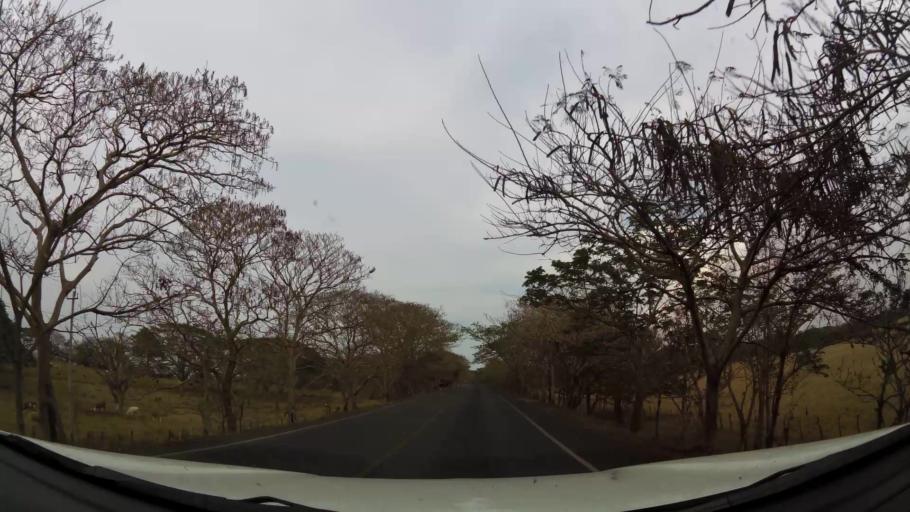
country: NI
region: Rivas
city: Cardenas
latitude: 11.2792
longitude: -85.6657
